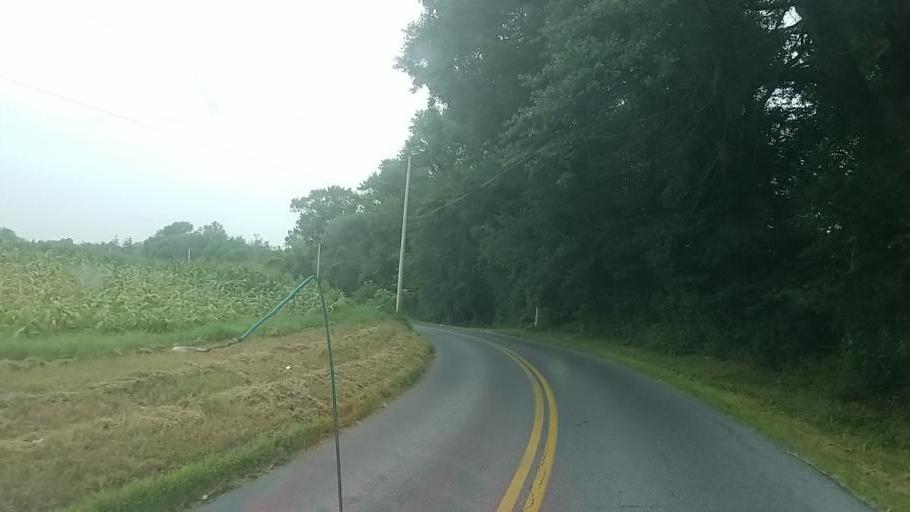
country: US
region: Delaware
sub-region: Sussex County
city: Selbyville
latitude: 38.4387
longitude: -75.1930
